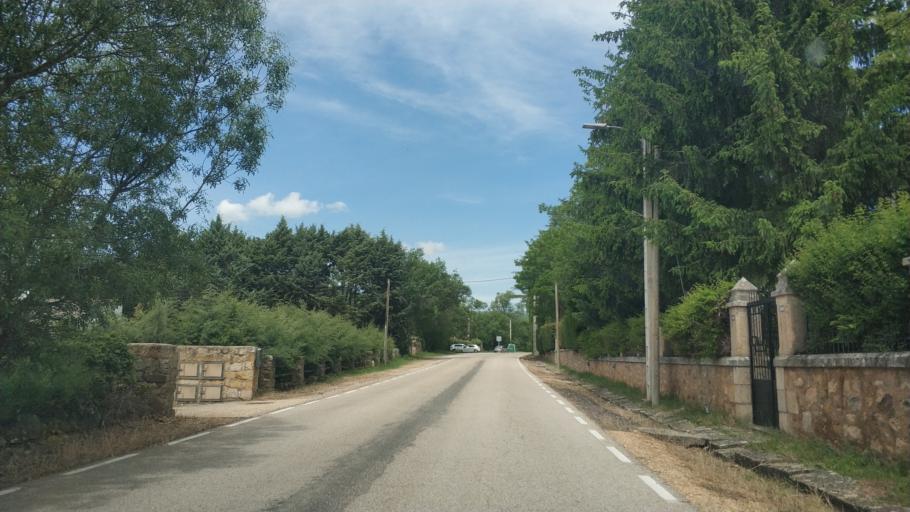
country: ES
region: Castille and Leon
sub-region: Provincia de Soria
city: Sotillo del Rincon
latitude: 41.9038
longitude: -2.6428
